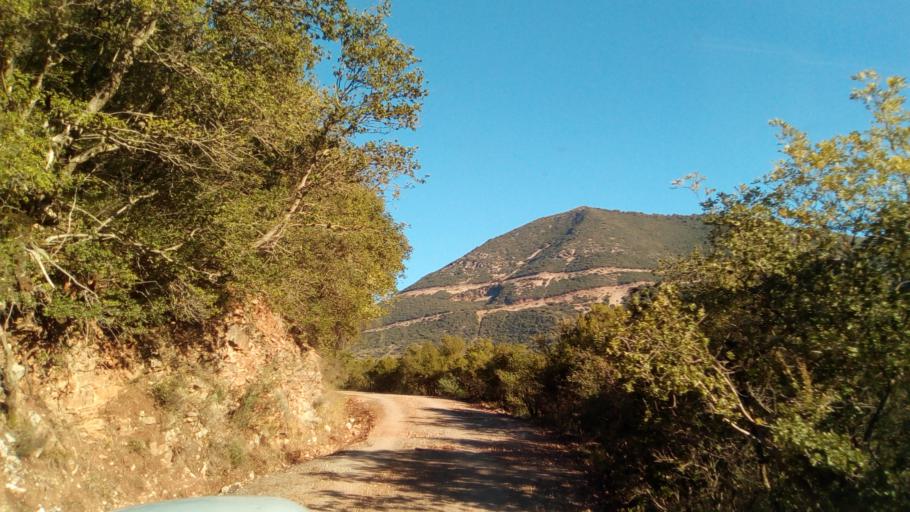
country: GR
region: West Greece
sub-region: Nomos Aitolias kai Akarnanias
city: Nafpaktos
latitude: 38.4674
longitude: 21.8670
